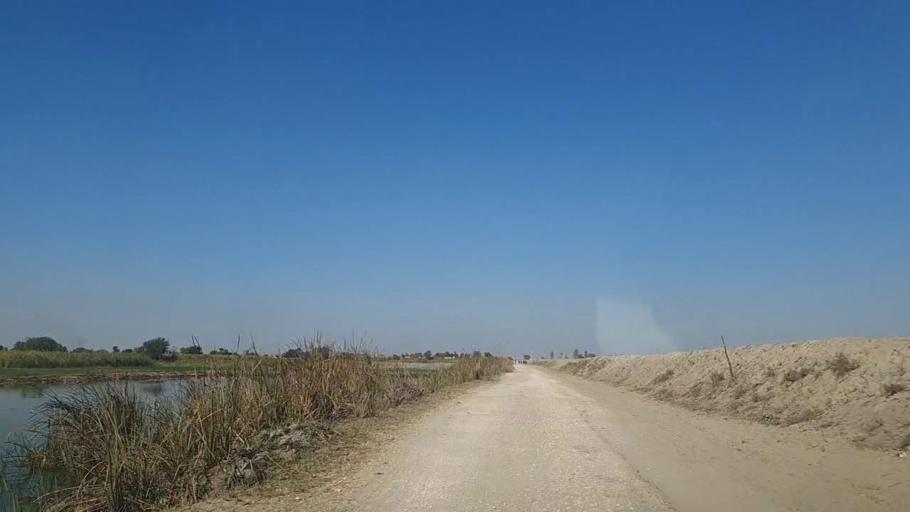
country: PK
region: Sindh
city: Sanghar
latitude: 26.2150
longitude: 68.9292
